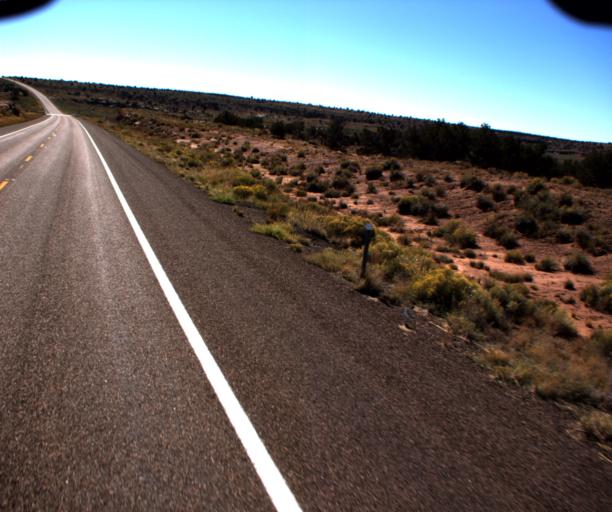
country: US
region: Arizona
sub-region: Apache County
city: Saint Johns
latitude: 34.6508
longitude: -109.7058
